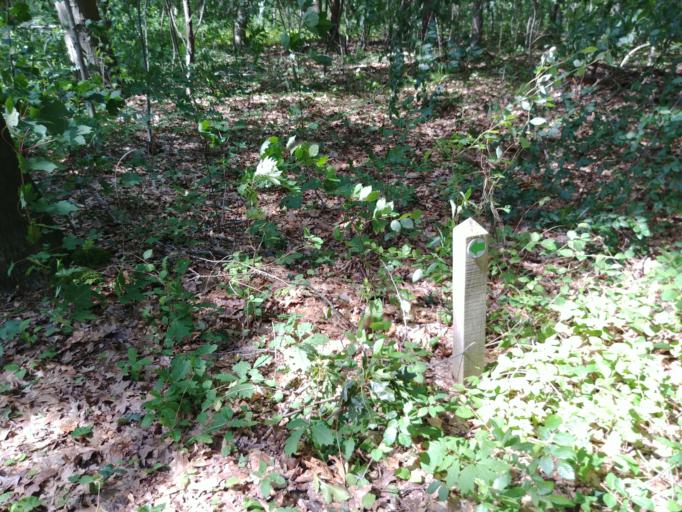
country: NL
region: North Holland
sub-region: Gemeente Heiloo
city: Heiloo
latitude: 52.6826
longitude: 4.6789
